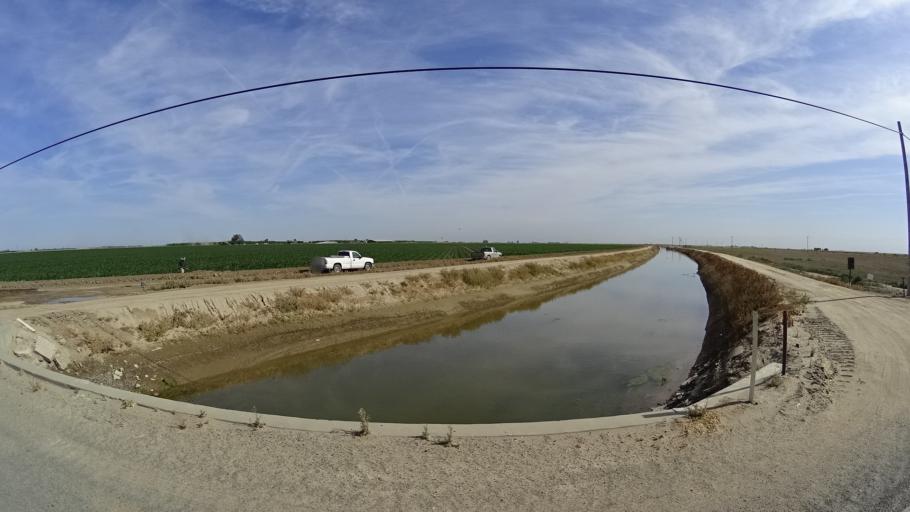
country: US
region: California
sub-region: Kings County
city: Home Garden
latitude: 36.3429
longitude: -119.5405
